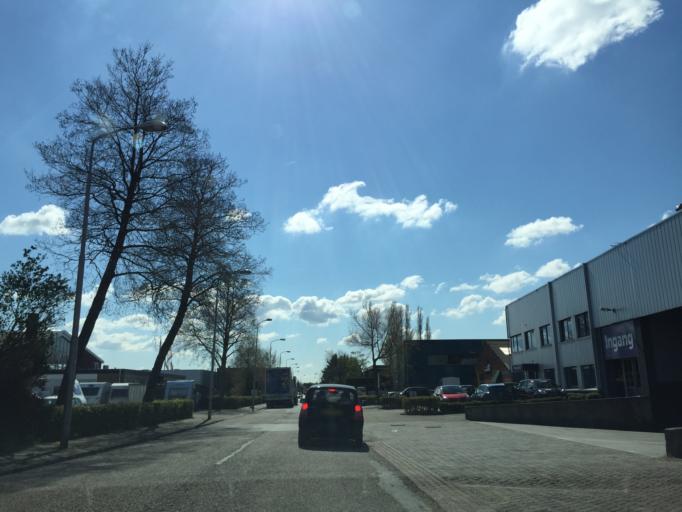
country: NL
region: South Holland
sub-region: Gemeente Pijnacker-Nootdorp
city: Pijnacker
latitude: 52.0267
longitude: 4.4368
